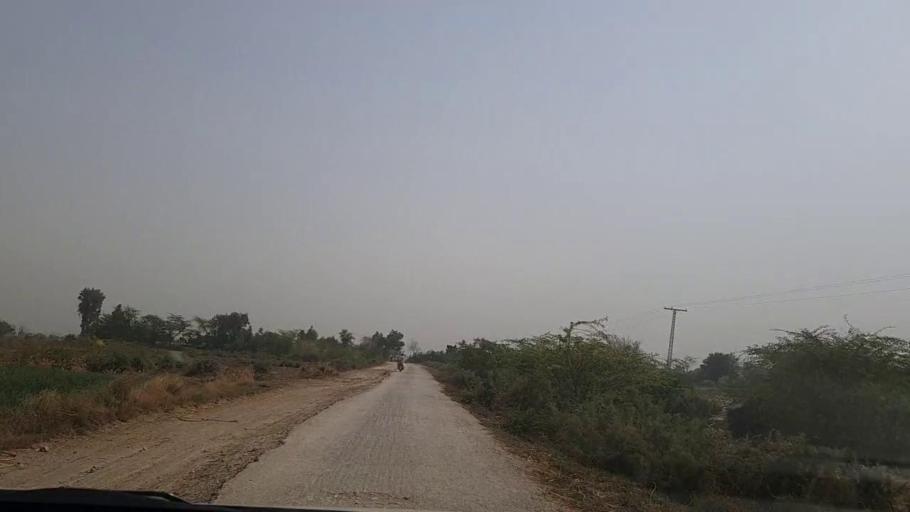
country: PK
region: Sindh
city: Pithoro
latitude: 25.4779
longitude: 69.2219
